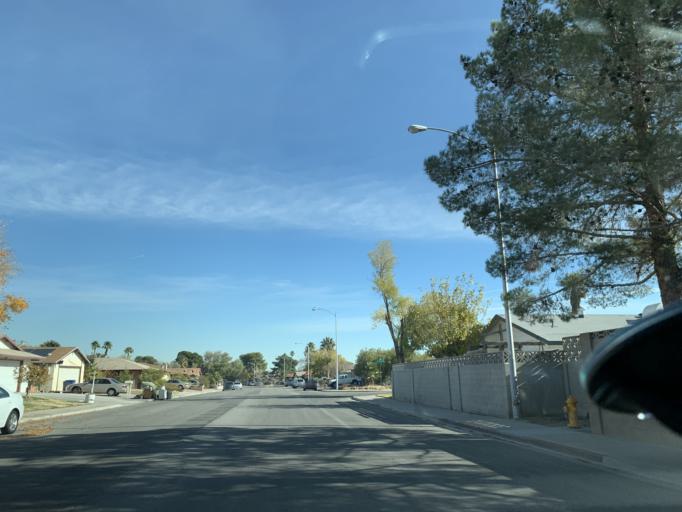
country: US
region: Nevada
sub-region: Clark County
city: Spring Valley
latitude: 36.1045
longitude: -115.2314
